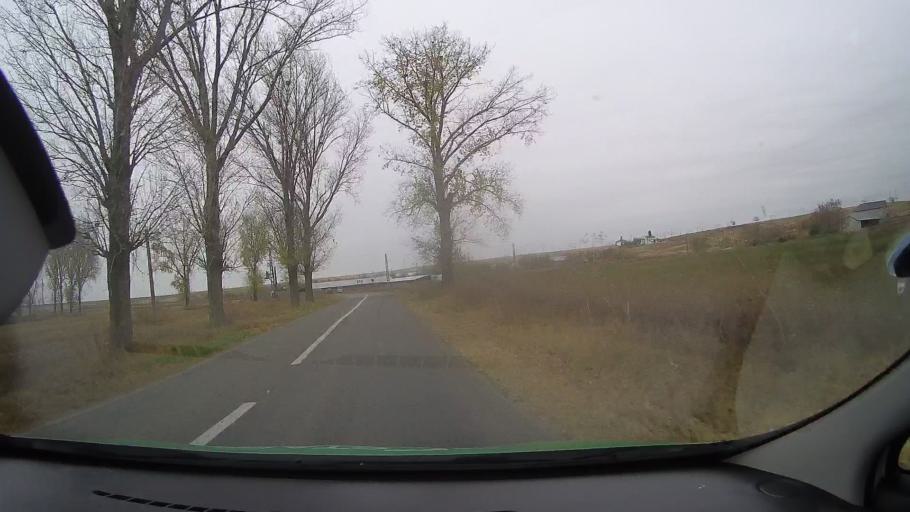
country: RO
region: Constanta
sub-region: Comuna Saraiu
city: Saraiu
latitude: 44.7256
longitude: 28.2206
